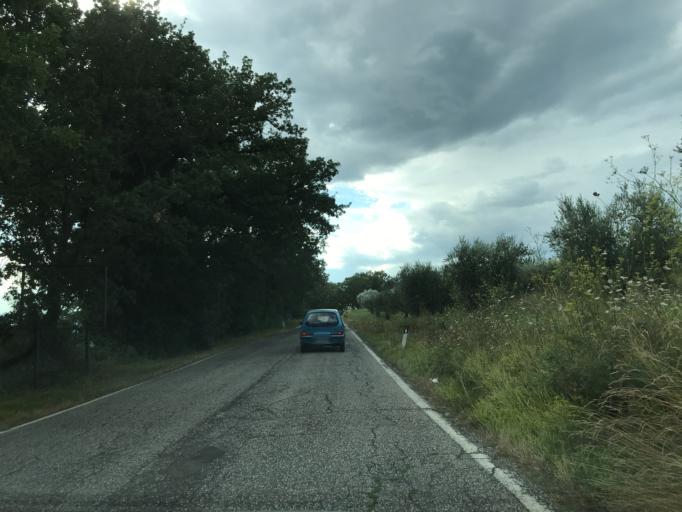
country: IT
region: Umbria
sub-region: Provincia di Terni
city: Guardea
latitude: 42.6392
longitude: 12.2909
